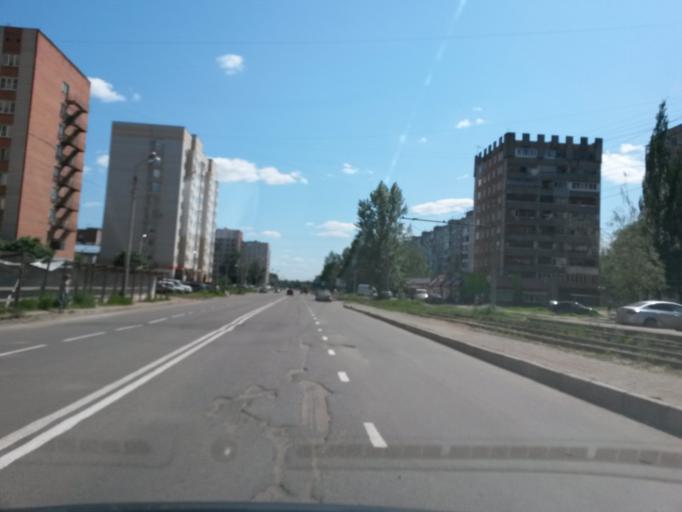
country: RU
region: Jaroslavl
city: Yaroslavl
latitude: 57.6902
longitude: 39.7592
